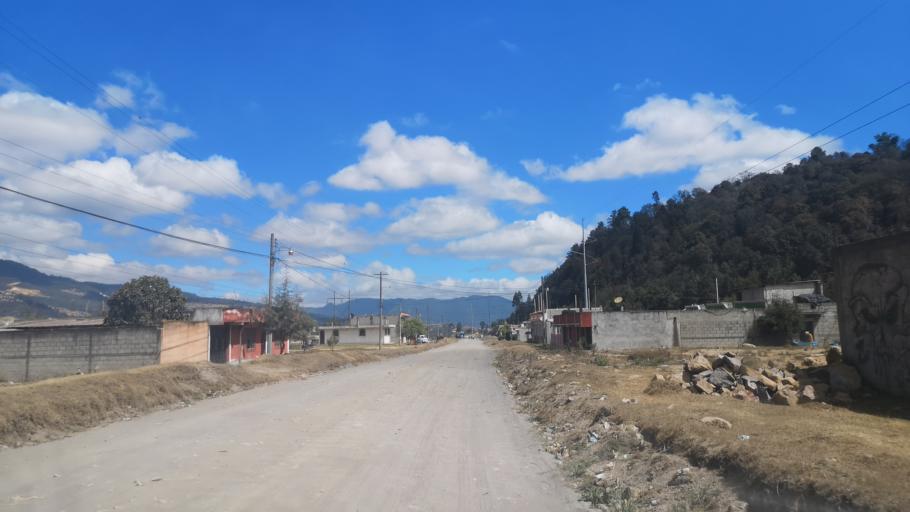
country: GT
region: Quetzaltenango
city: Almolonga
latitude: 14.7852
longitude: -91.5362
